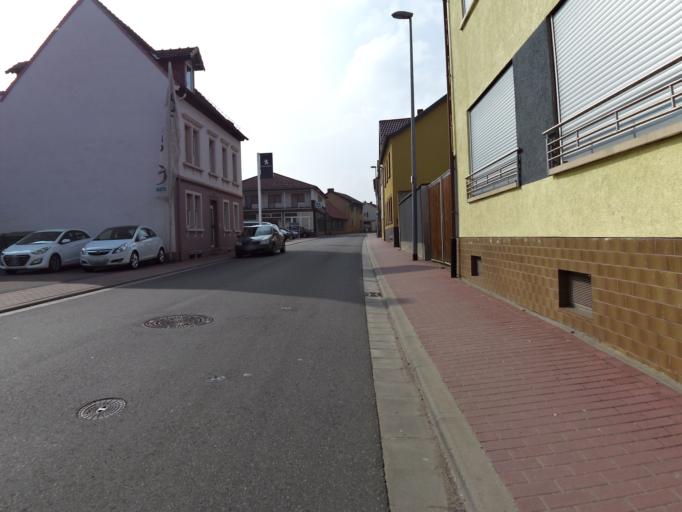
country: DE
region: Rheinland-Pfalz
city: Eisenberg
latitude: 49.5597
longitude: 8.0792
